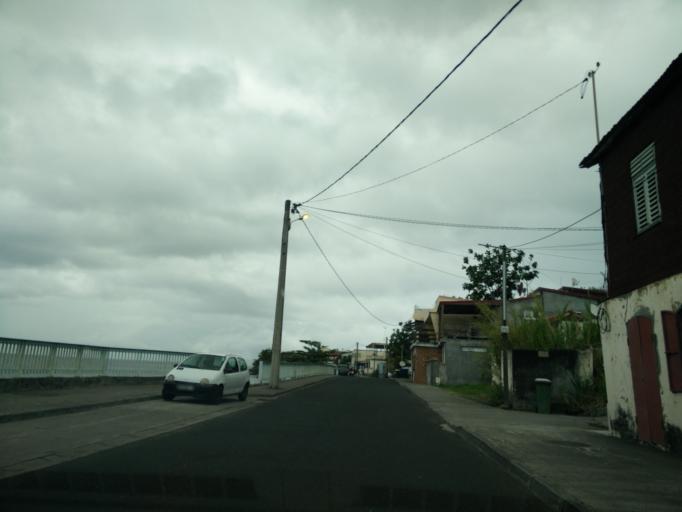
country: MQ
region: Martinique
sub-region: Martinique
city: Saint-Pierre
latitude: 14.7986
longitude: -61.2226
